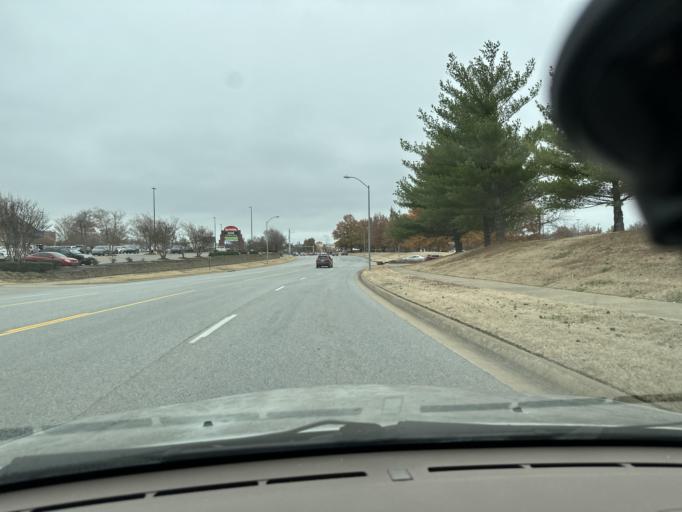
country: US
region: Arkansas
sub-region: Washington County
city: Johnson
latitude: 36.1240
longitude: -94.1528
